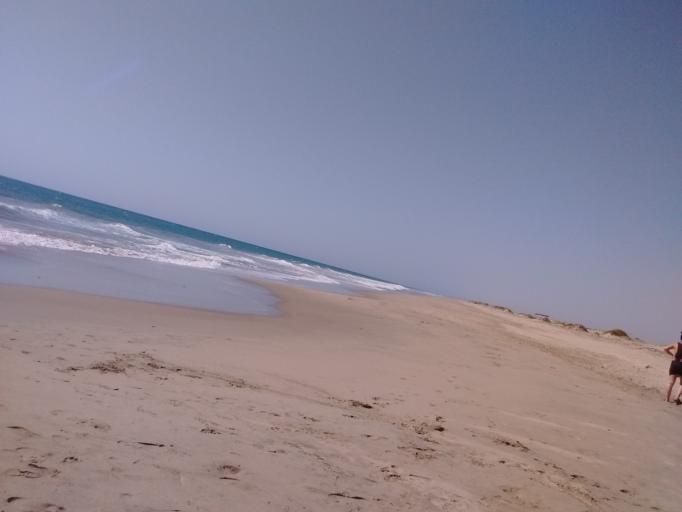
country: PE
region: Piura
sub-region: Provincia de Talara
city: Mancora
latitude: -4.0972
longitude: -81.0504
